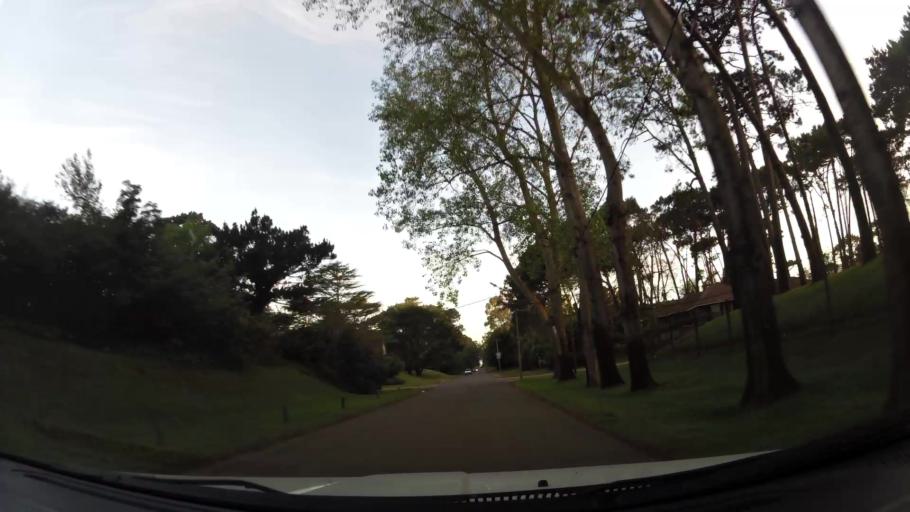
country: UY
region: Maldonado
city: Punta del Este
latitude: -34.9354
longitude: -54.9307
